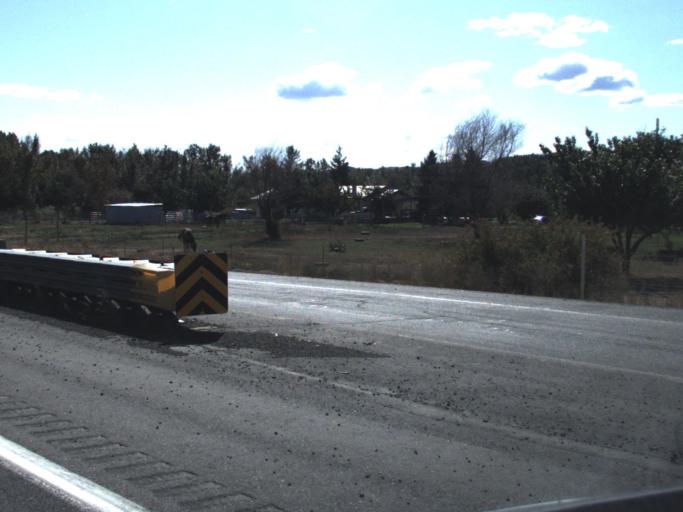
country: US
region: Washington
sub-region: Yakima County
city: Tieton
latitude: 46.7157
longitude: -120.6753
